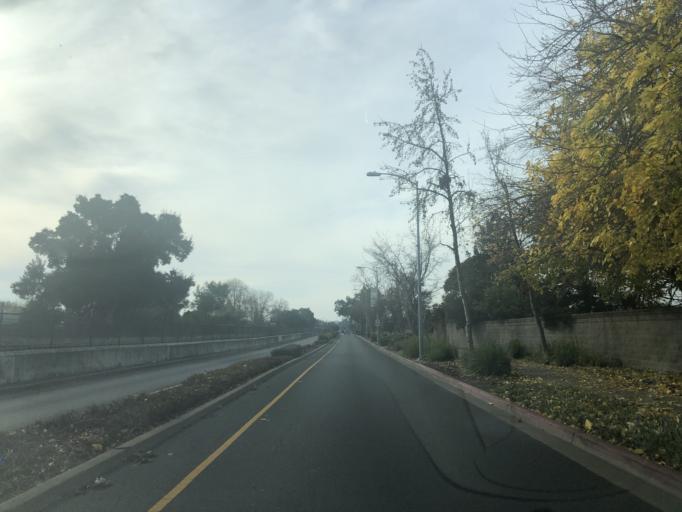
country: US
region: California
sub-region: Contra Costa County
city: Concord
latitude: 37.9984
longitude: -122.0287
